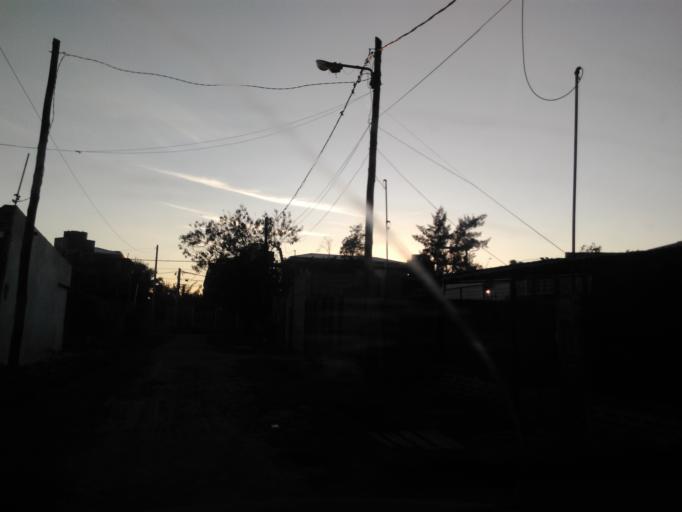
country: AR
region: Chaco
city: Resistencia
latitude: -27.4783
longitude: -58.9890
